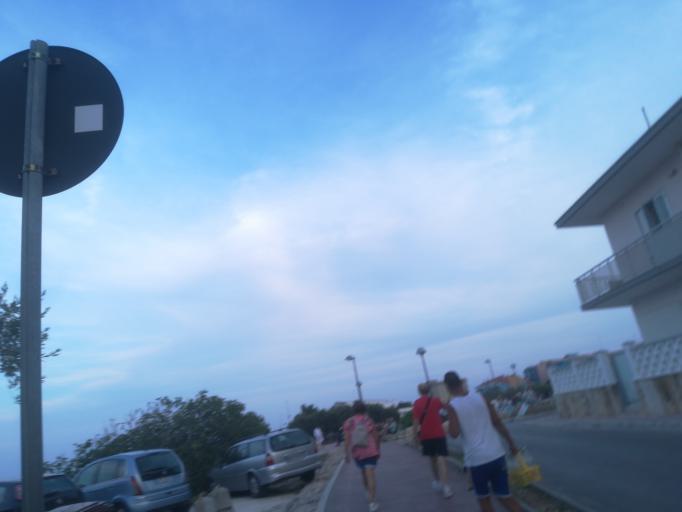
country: IT
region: Apulia
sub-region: Provincia di Bari
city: Monopoli
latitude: 40.9475
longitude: 17.3072
